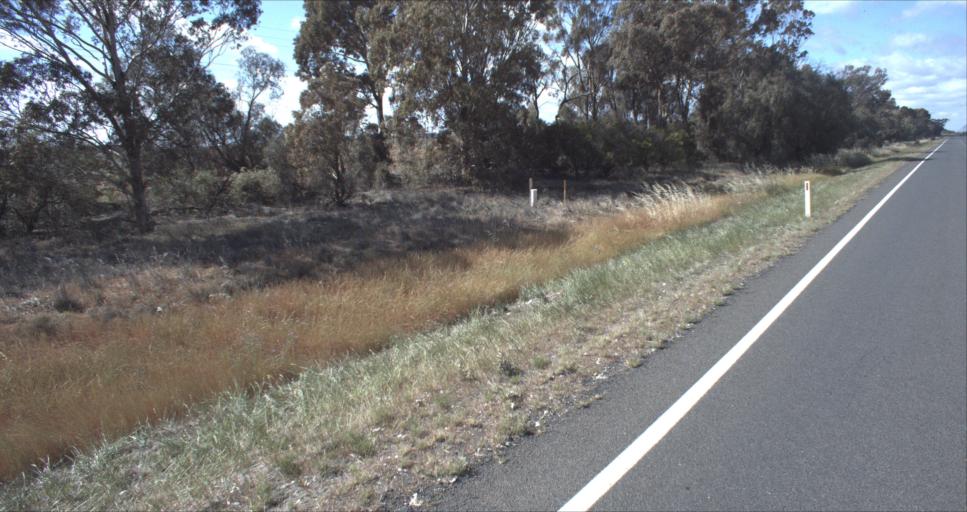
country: AU
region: New South Wales
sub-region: Murrumbidgee Shire
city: Darlington Point
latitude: -34.5331
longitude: 146.1736
